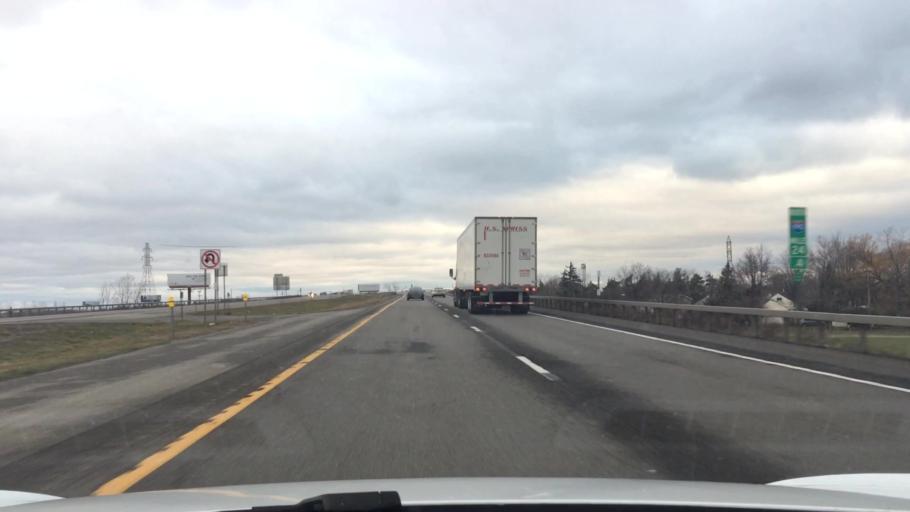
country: US
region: New York
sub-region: Niagara County
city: Niagara Falls
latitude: 43.1145
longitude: -78.9982
